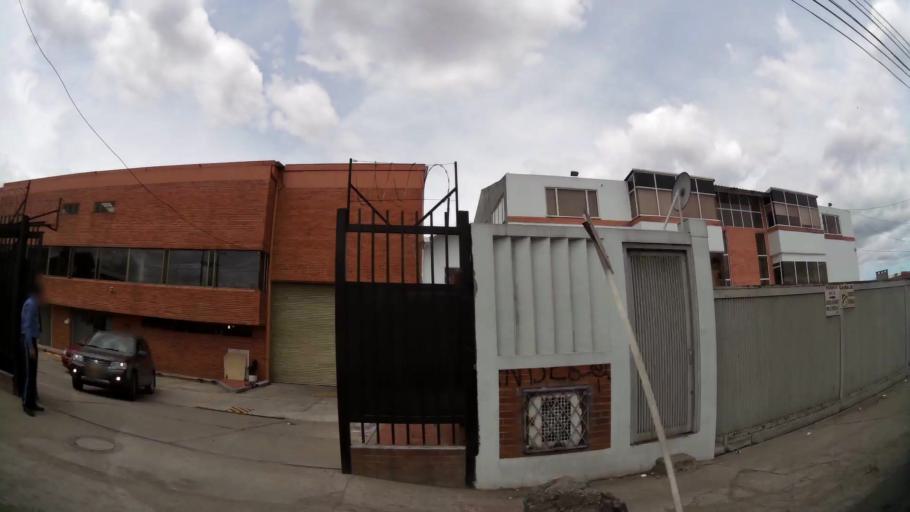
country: CO
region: Cundinamarca
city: Funza
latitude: 4.7090
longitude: -74.1388
